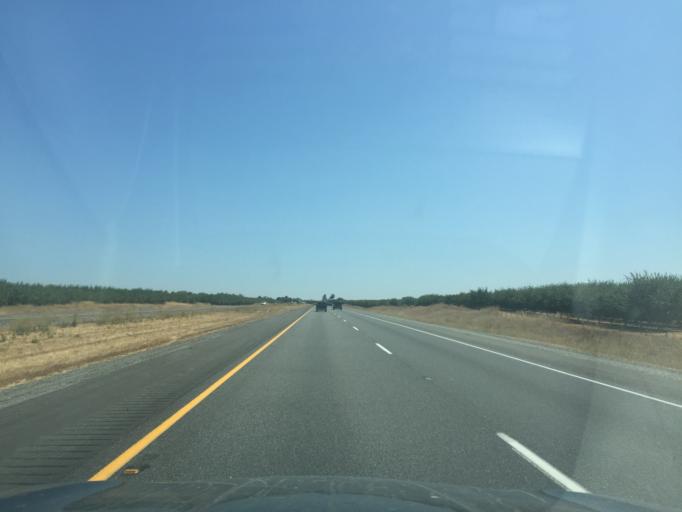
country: US
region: California
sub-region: Tehama County
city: Gerber
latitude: 40.0208
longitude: -122.2094
